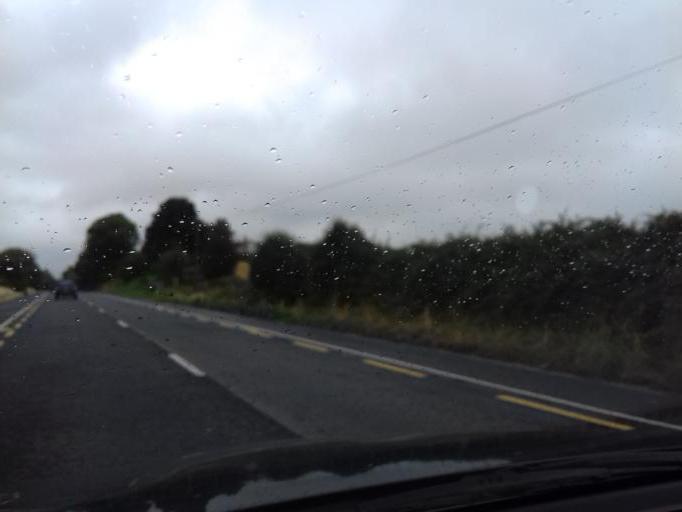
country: IE
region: Leinster
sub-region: County Carlow
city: Bagenalstown
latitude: 52.7524
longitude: -6.9620
